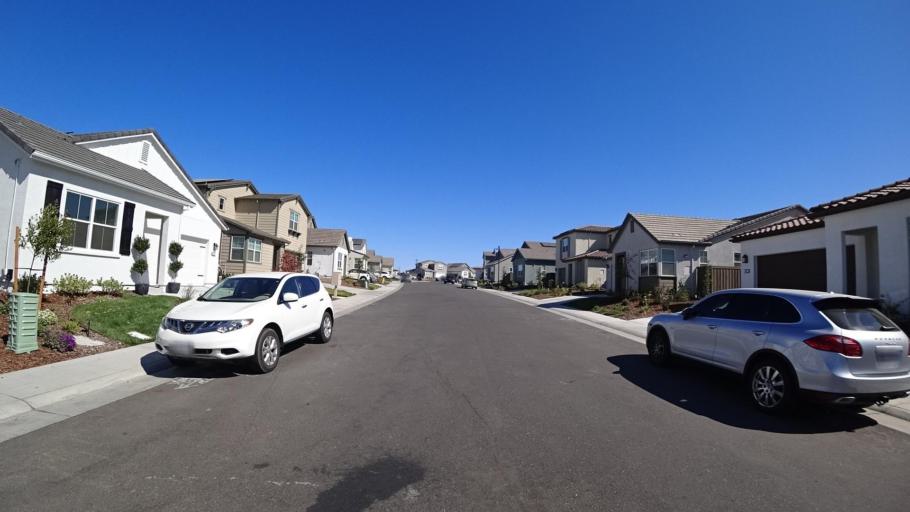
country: US
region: California
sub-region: Placer County
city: Rocklin
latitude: 38.8306
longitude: -121.2653
